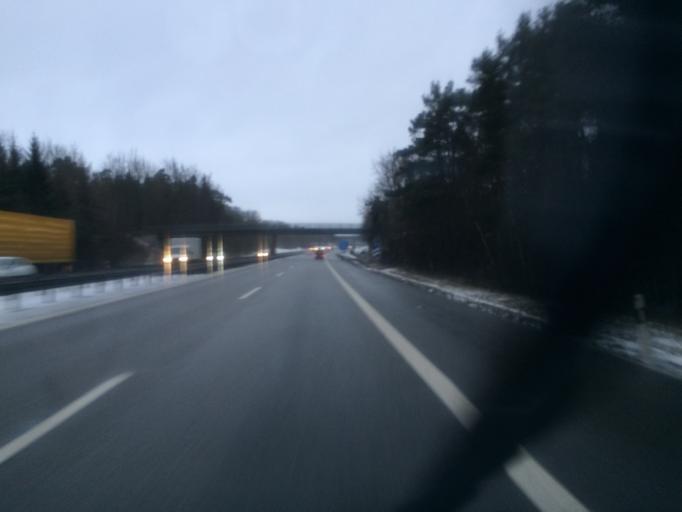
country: DE
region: Bavaria
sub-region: Upper Palatinate
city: Wackersdorf
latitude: 49.3355
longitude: 12.1509
